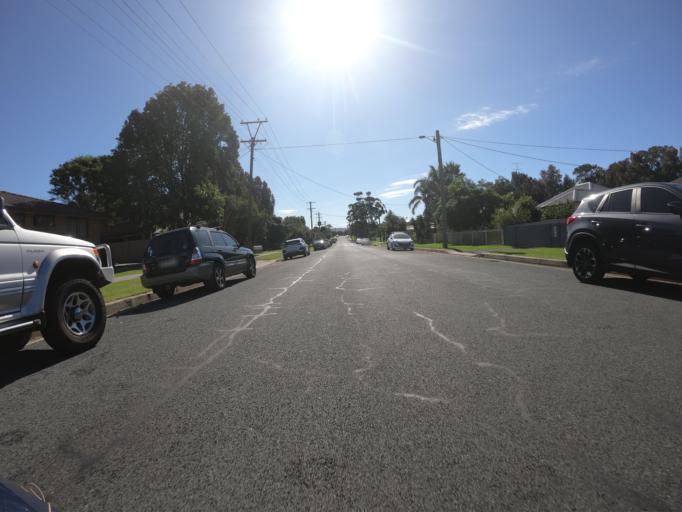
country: AU
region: New South Wales
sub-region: Wollongong
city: East Corrimal
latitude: -34.3716
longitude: 150.9079
